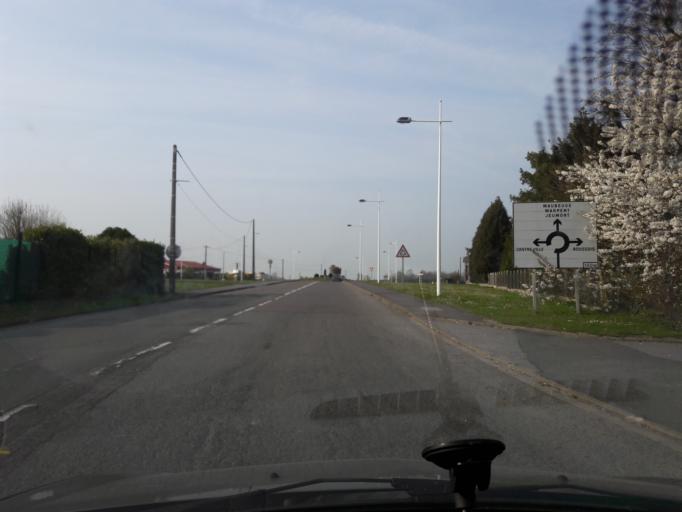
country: FR
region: Nord-Pas-de-Calais
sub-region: Departement du Nord
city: Recquignies
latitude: 50.2879
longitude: 4.0260
